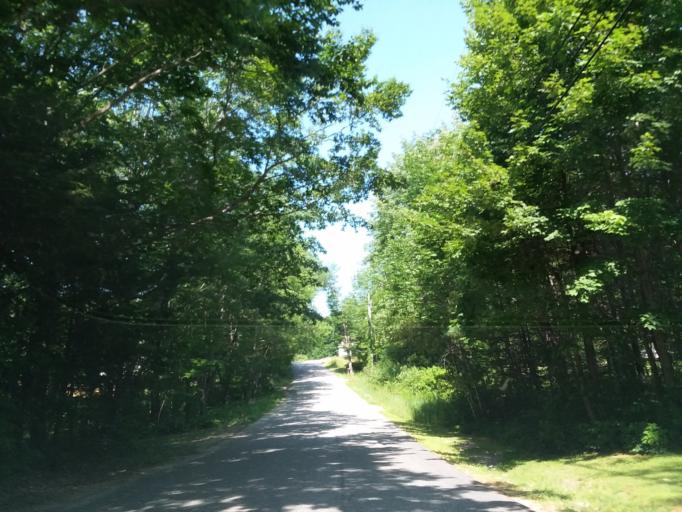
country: US
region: Maine
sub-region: Kennebec County
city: Monmouth
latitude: 44.2804
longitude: -70.0183
